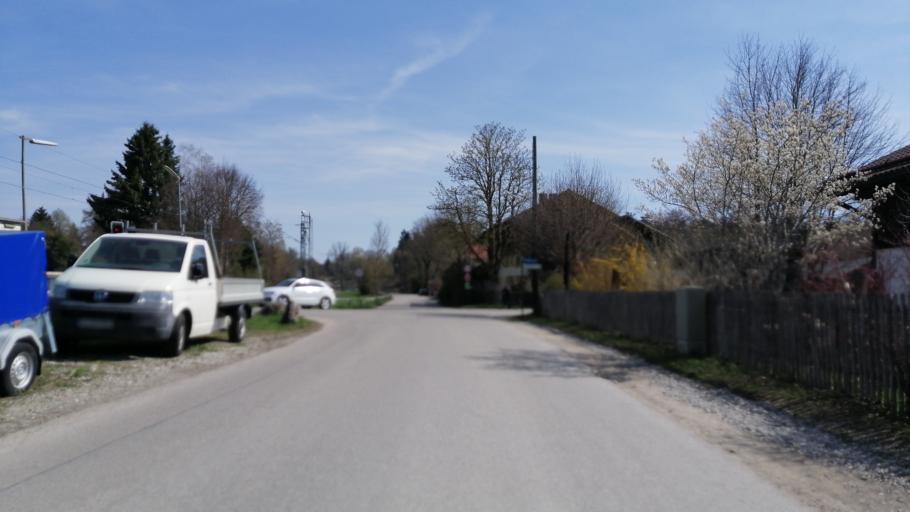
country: DE
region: Bavaria
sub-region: Upper Bavaria
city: Oberhaching
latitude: 48.0139
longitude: 11.5860
